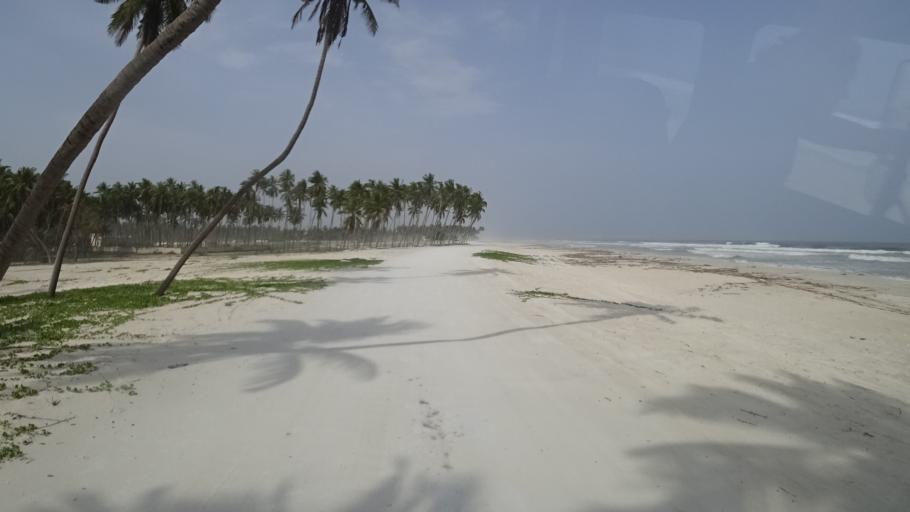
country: OM
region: Zufar
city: Salalah
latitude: 17.0019
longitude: 54.1169
